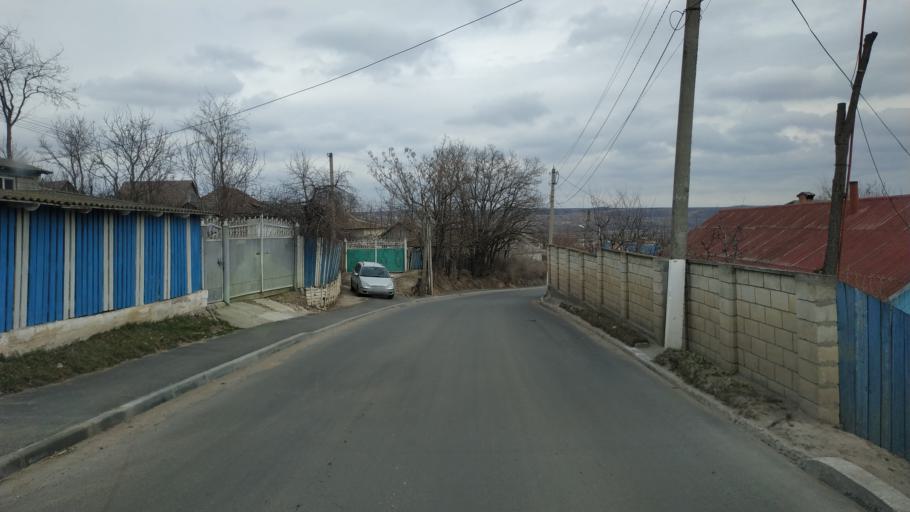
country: MD
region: Laloveni
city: Ialoveni
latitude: 46.8672
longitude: 28.7614
